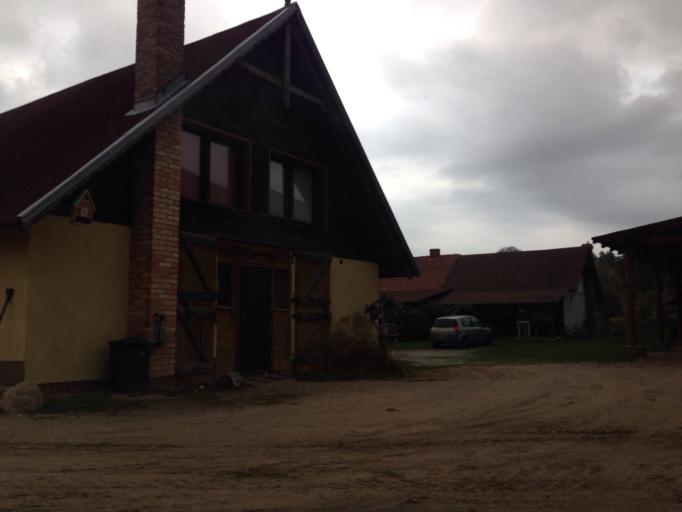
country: PL
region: Kujawsko-Pomorskie
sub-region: Powiat brodnicki
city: Gorzno
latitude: 53.2710
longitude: 19.7032
